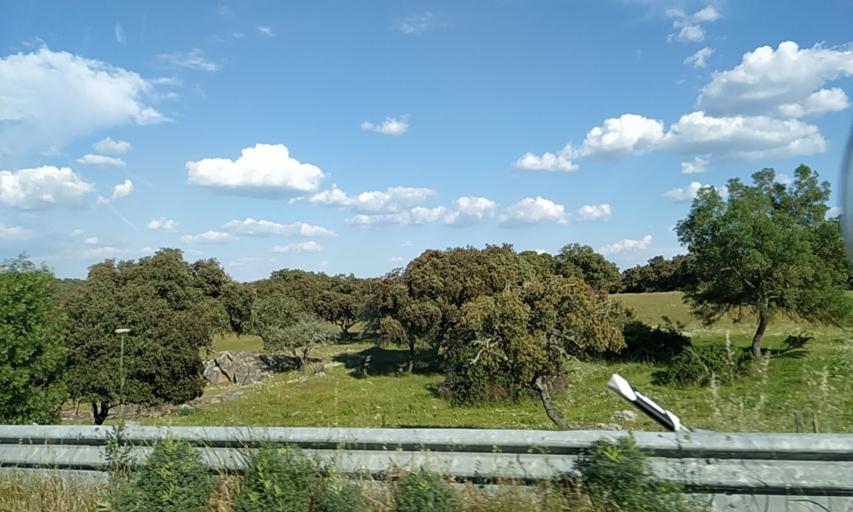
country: PT
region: Portalegre
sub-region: Fronteira
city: Fronteira
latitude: 38.9940
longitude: -7.4732
